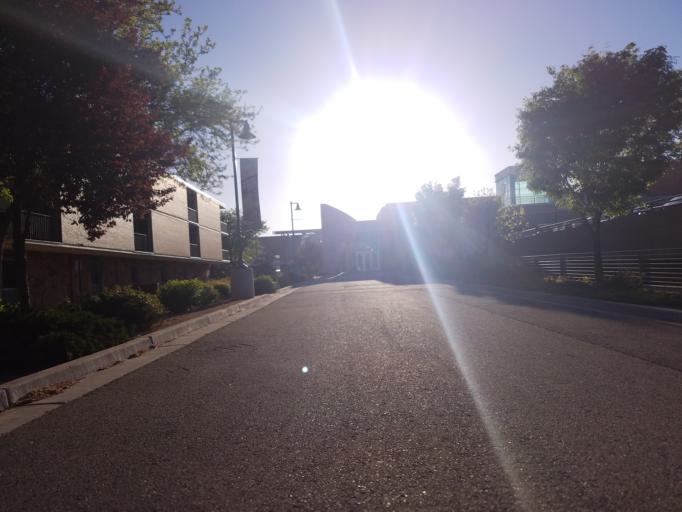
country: US
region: Colorado
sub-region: Mesa County
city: Grand Junction
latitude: 39.0828
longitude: -108.5529
